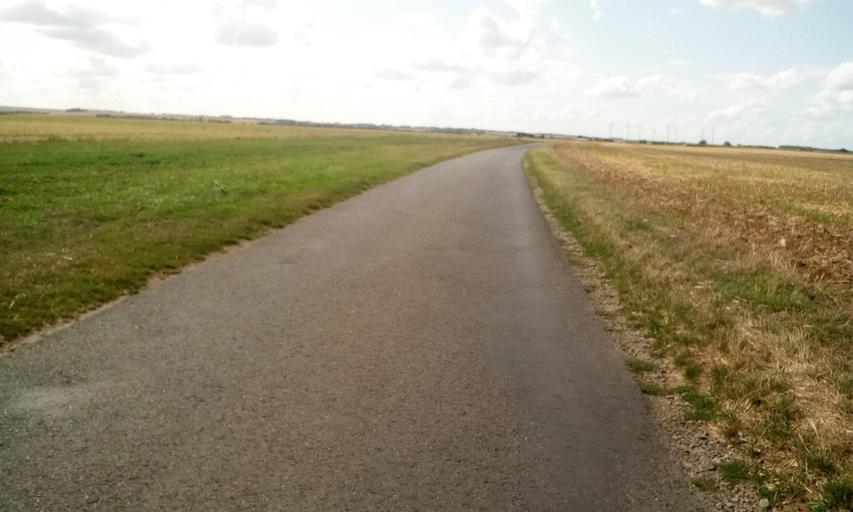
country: FR
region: Lower Normandy
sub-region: Departement du Calvados
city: Saint-Sylvain
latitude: 49.0746
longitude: -0.2038
